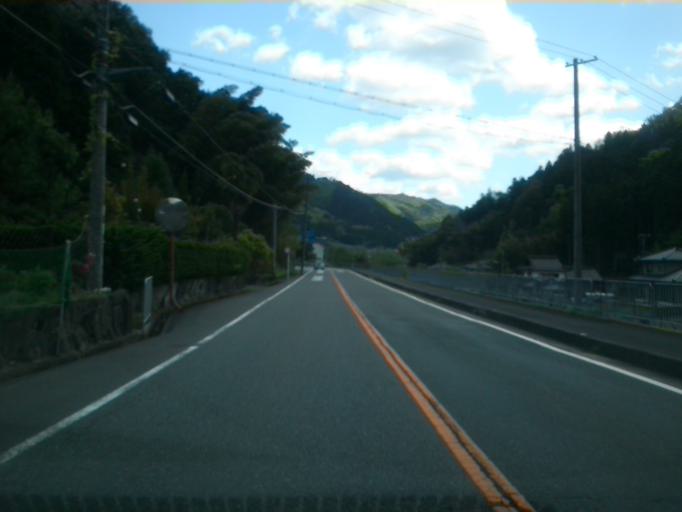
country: JP
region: Kyoto
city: Fukuchiyama
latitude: 35.3367
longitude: 135.0697
